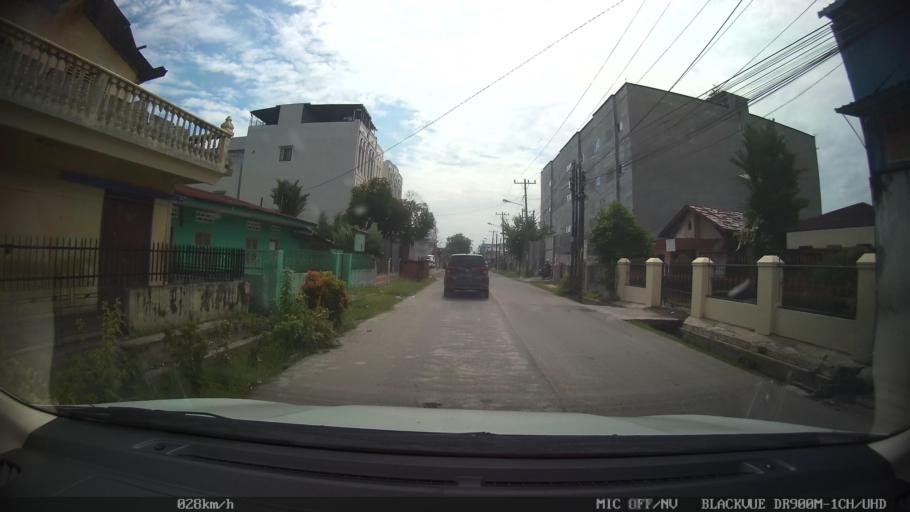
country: ID
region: North Sumatra
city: Medan
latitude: 3.5873
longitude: 98.7124
